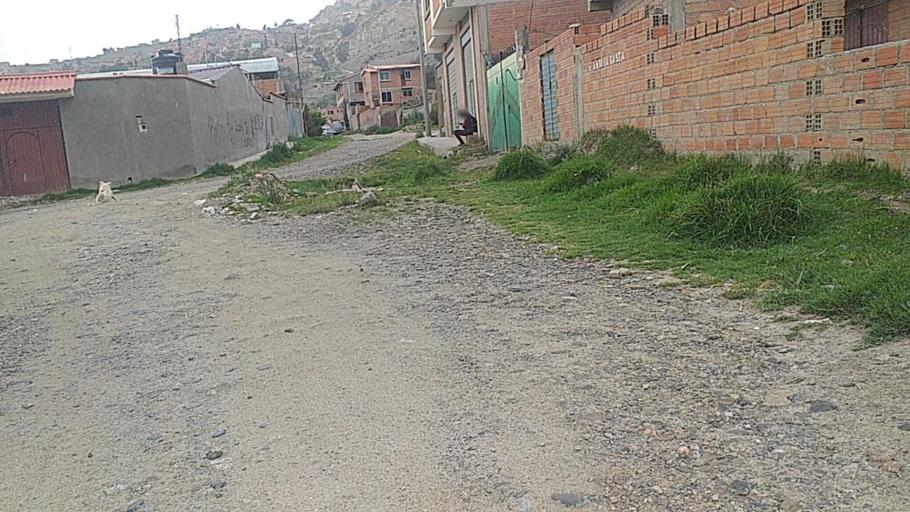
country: BO
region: La Paz
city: La Paz
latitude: -16.4962
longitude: -68.0868
